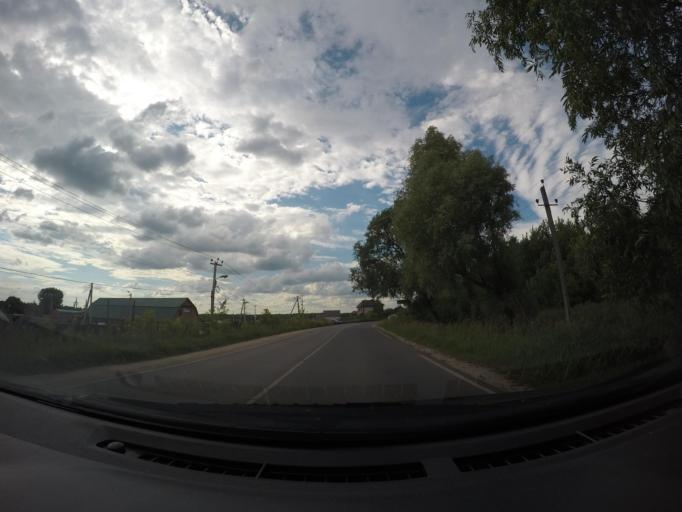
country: RU
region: Moskovskaya
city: Rechitsy
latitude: 55.6073
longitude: 38.5255
